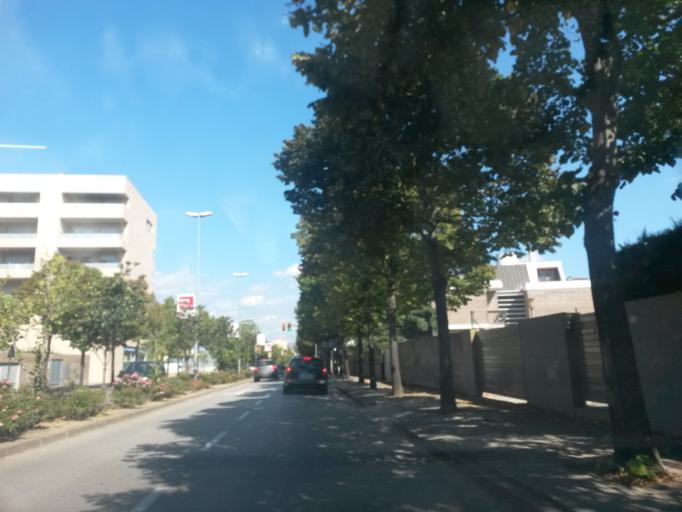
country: ES
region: Catalonia
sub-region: Provincia de Girona
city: Salt
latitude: 41.9678
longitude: 2.7874
